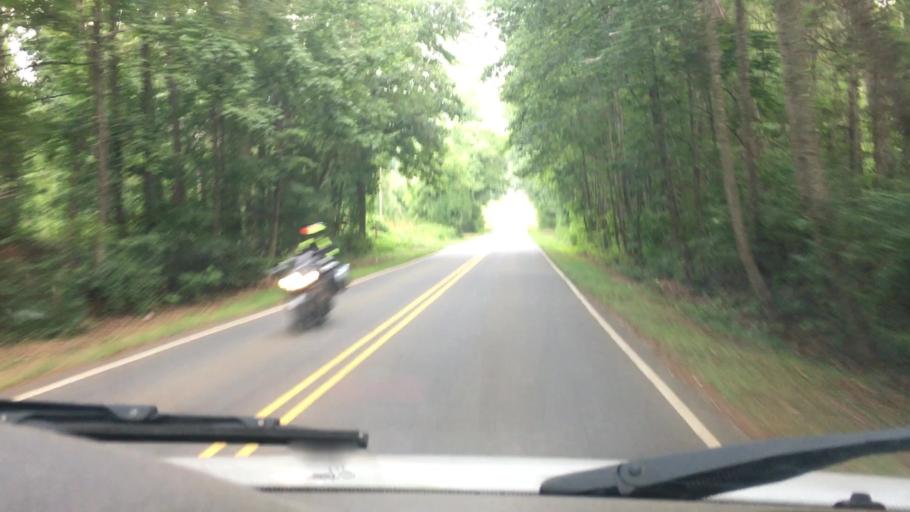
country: US
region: North Carolina
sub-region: Mecklenburg County
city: Huntersville
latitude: 35.4015
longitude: -80.9204
